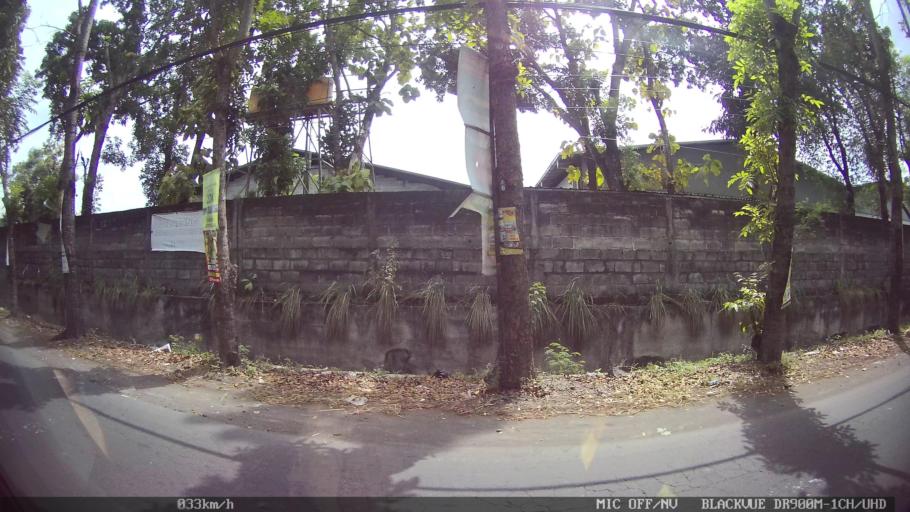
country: ID
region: Daerah Istimewa Yogyakarta
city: Depok
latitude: -7.8048
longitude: 110.4468
